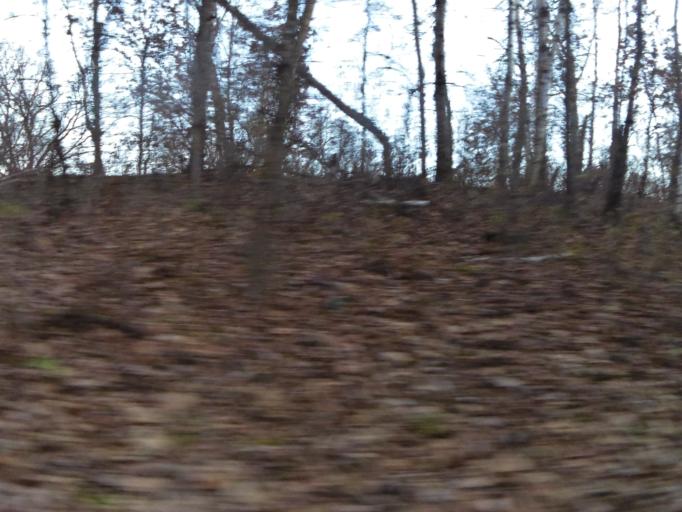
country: US
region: Minnesota
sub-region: Washington County
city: Grant
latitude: 45.0990
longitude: -92.8717
